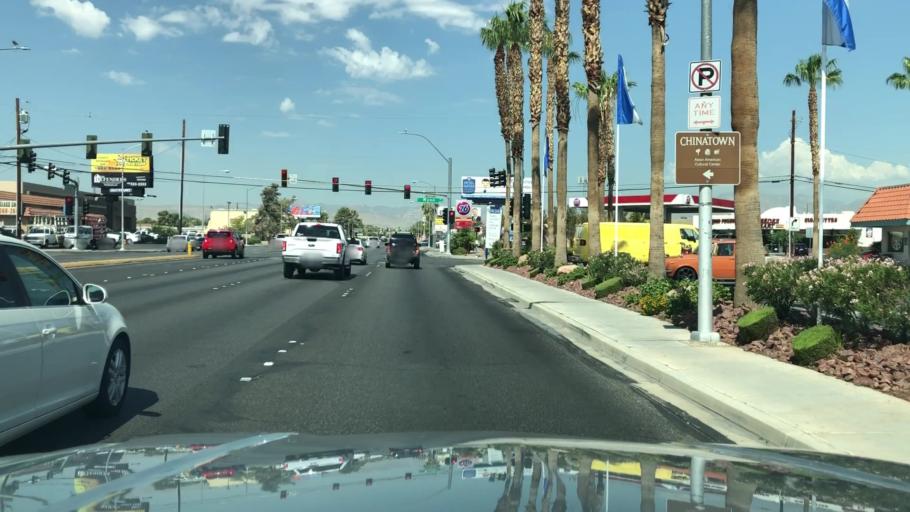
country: US
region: Nevada
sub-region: Clark County
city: Spring Valley
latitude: 36.1303
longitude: -115.1941
